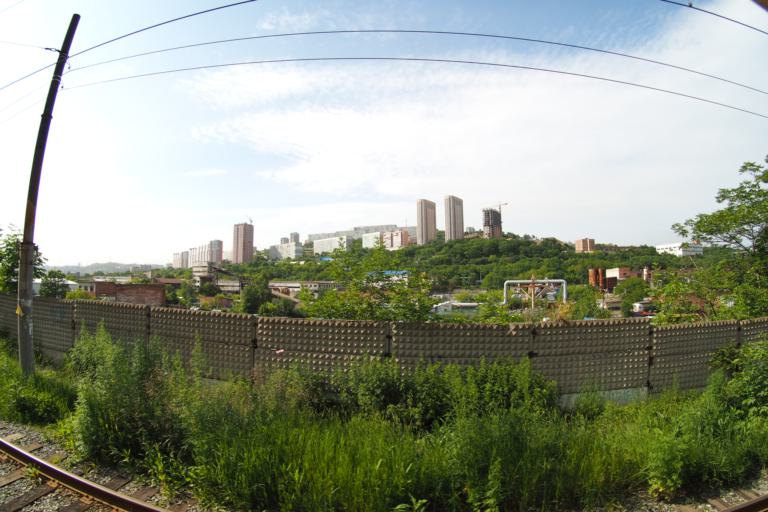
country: RU
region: Primorskiy
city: Vladivostok
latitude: 43.0971
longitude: 131.9614
